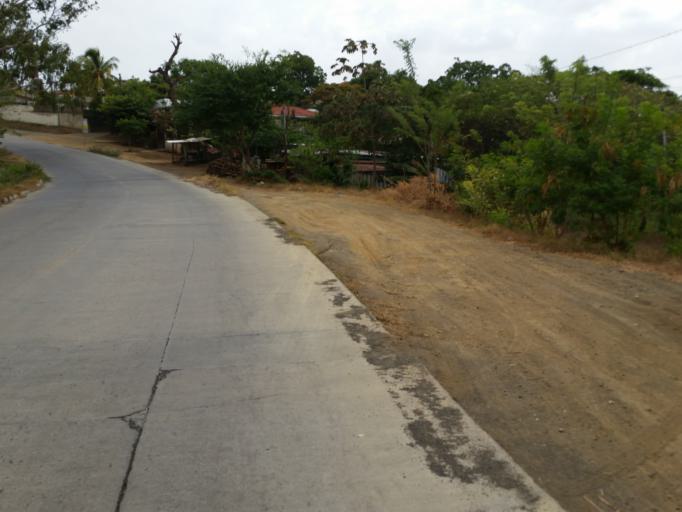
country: NI
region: Managua
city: Managua
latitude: 12.0812
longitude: -86.2447
